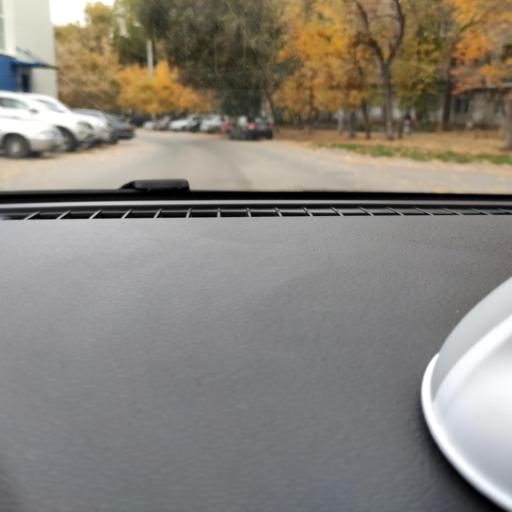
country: RU
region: Samara
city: Samara
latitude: 53.2067
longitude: 50.1814
